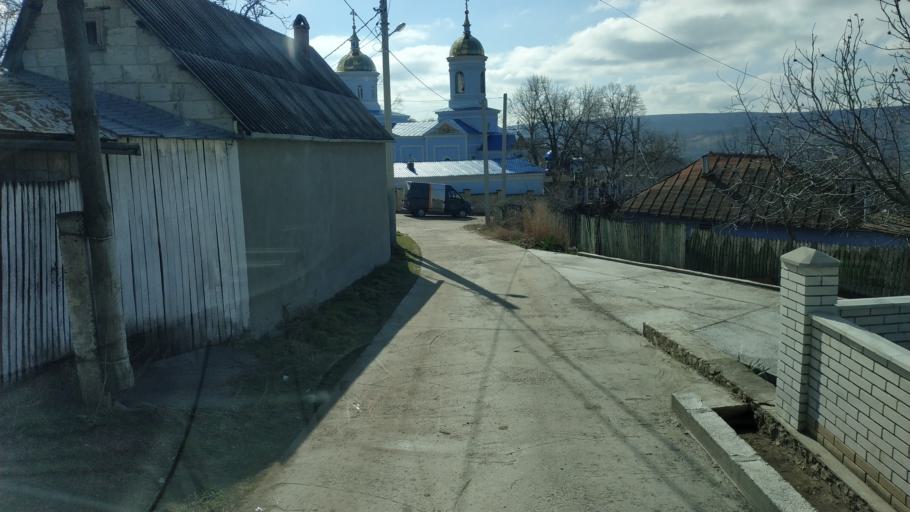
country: MD
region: Straseni
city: Straseni
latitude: 47.0210
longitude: 28.5487
